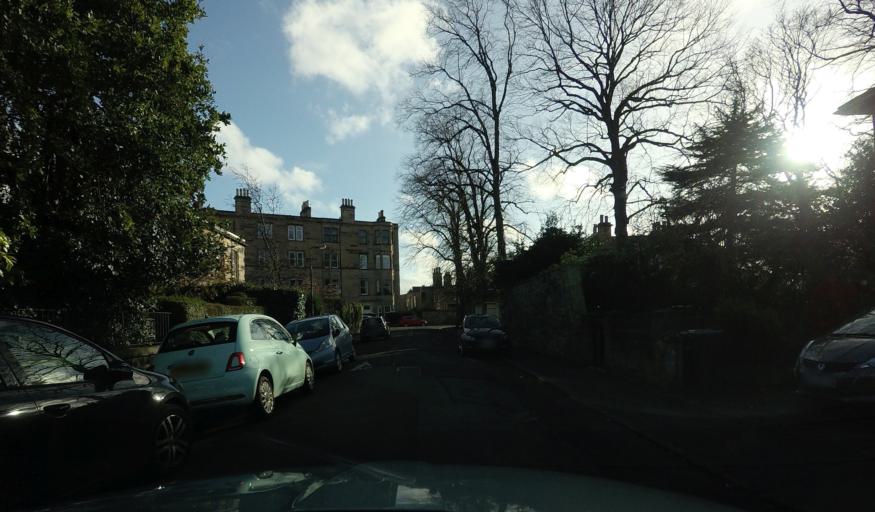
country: GB
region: Scotland
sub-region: Edinburgh
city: Edinburgh
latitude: 55.9772
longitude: -3.2008
